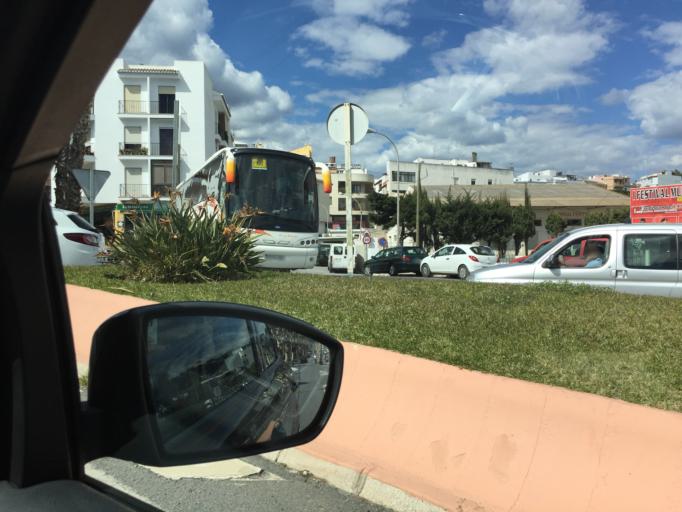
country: ES
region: Andalusia
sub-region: Provincia de Granada
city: Almunecar
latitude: 36.7371
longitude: -3.6882
